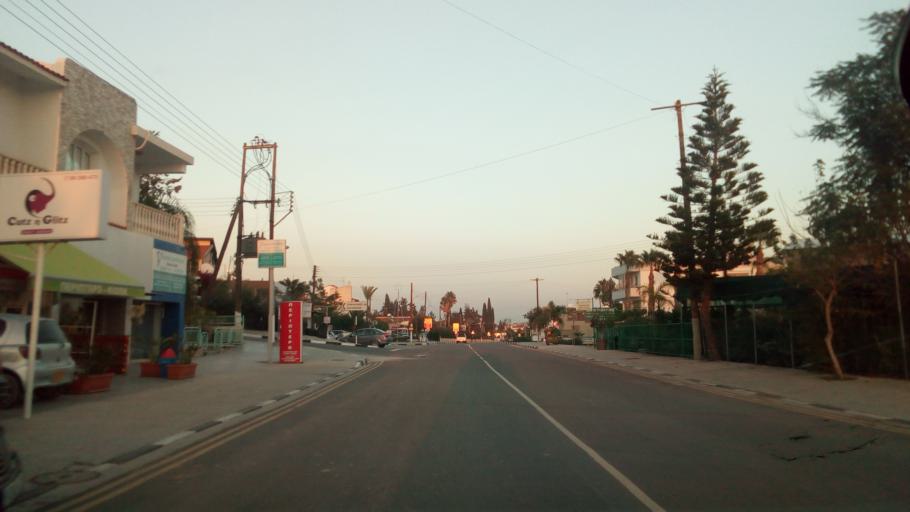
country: CY
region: Larnaka
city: Kofinou
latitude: 34.8523
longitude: 33.4537
